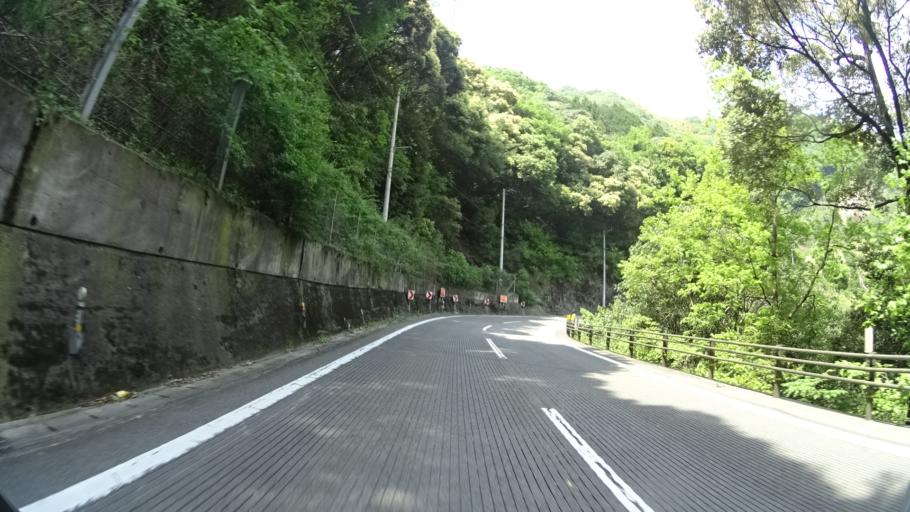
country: JP
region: Ehime
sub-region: Shikoku-chuo Shi
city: Matsuyama
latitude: 33.8741
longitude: 132.8324
